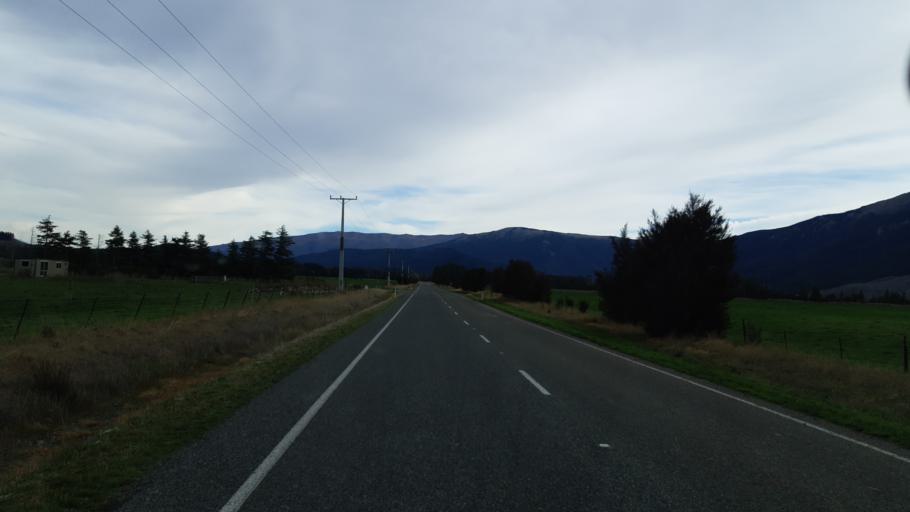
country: NZ
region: Tasman
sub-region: Tasman District
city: Brightwater
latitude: -41.6532
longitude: 173.2702
